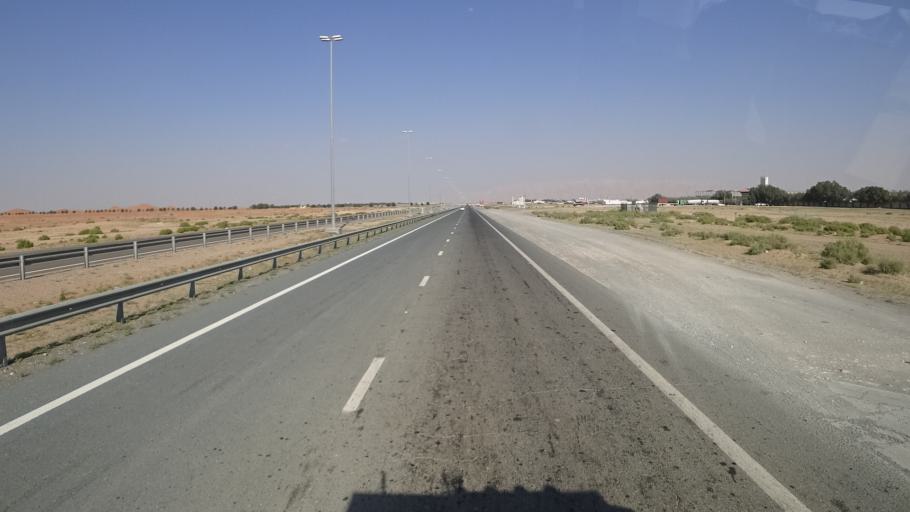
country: AE
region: Abu Dhabi
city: Al Ain
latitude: 24.0438
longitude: 55.5908
